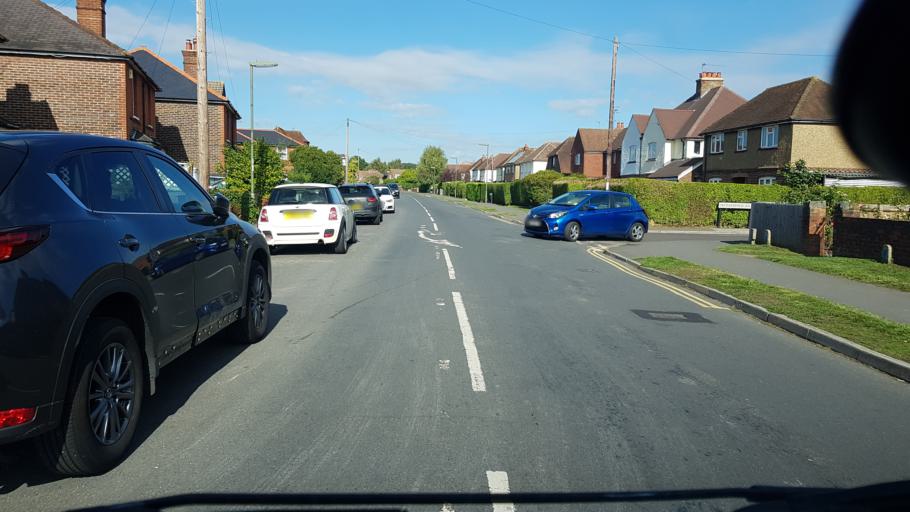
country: GB
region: England
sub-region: Surrey
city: Godalming
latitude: 51.1991
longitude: -0.6028
